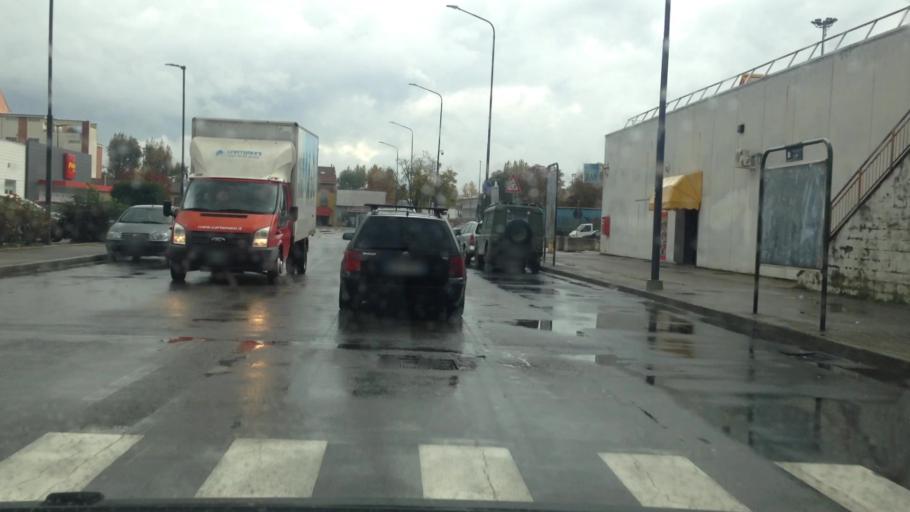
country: IT
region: Piedmont
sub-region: Provincia di Asti
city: Asti
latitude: 44.9068
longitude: 8.2230
